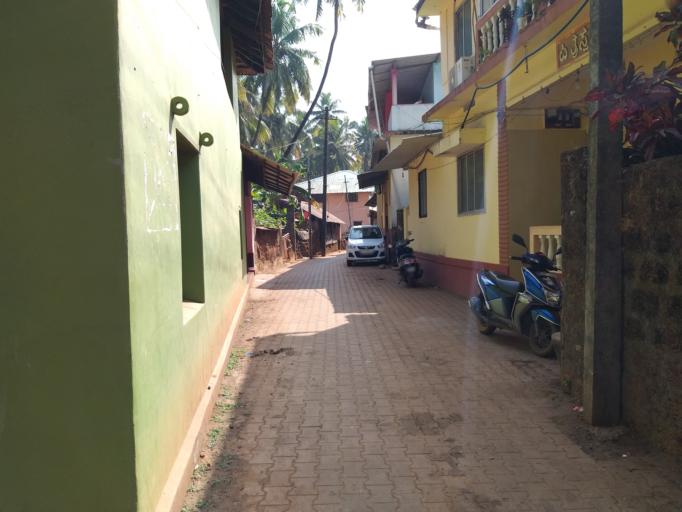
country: IN
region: Karnataka
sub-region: Uttar Kannada
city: Gokarna
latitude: 14.5422
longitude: 74.3182
